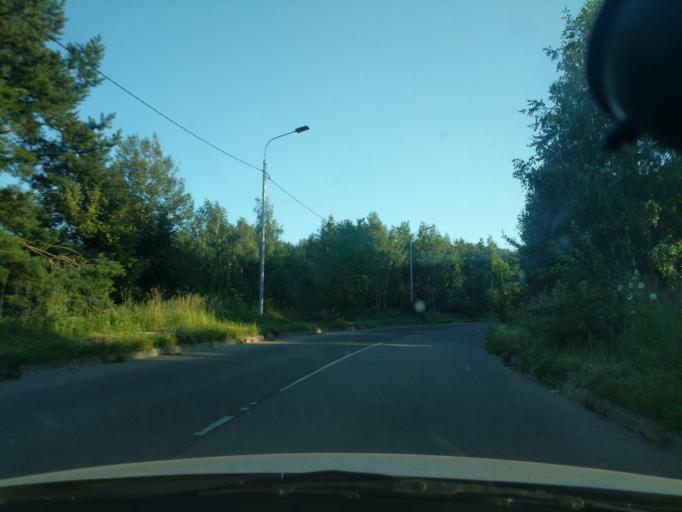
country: RU
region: Moskovskaya
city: Pushchino
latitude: 54.8392
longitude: 37.6415
